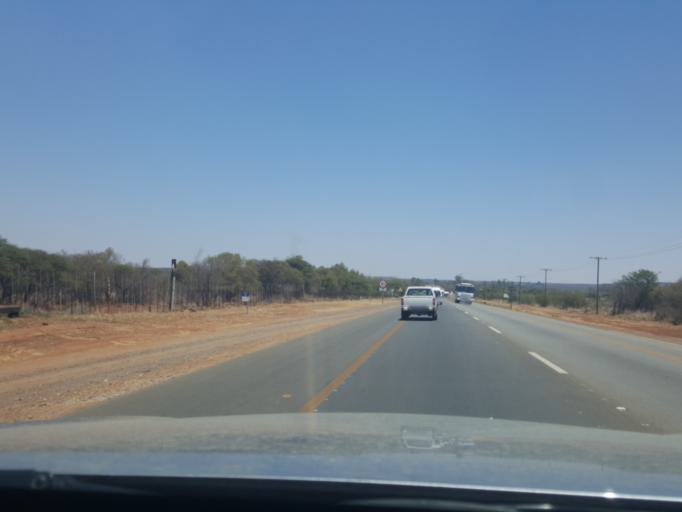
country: ZA
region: North-West
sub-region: Ngaka Modiri Molema District Municipality
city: Zeerust
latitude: -25.5570
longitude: 26.0666
